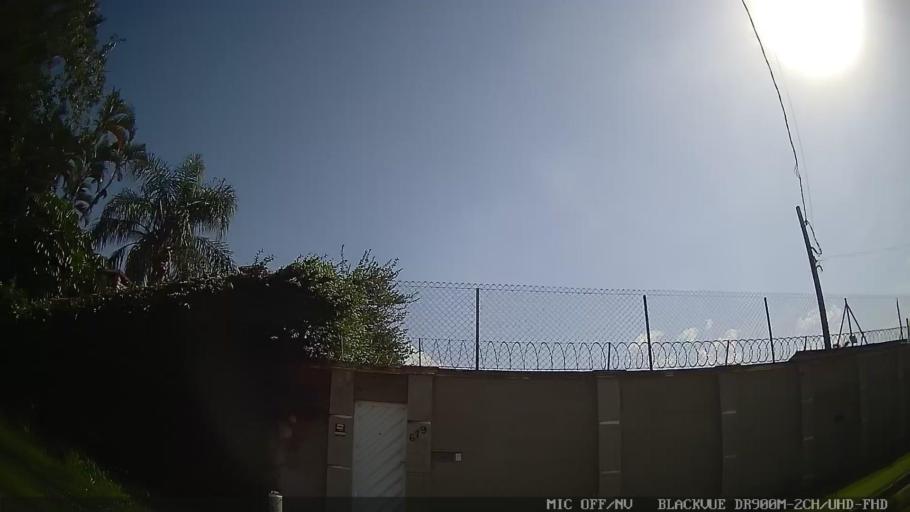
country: BR
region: Sao Paulo
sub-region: Guaruja
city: Guaruja
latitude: -23.9724
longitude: -46.1923
